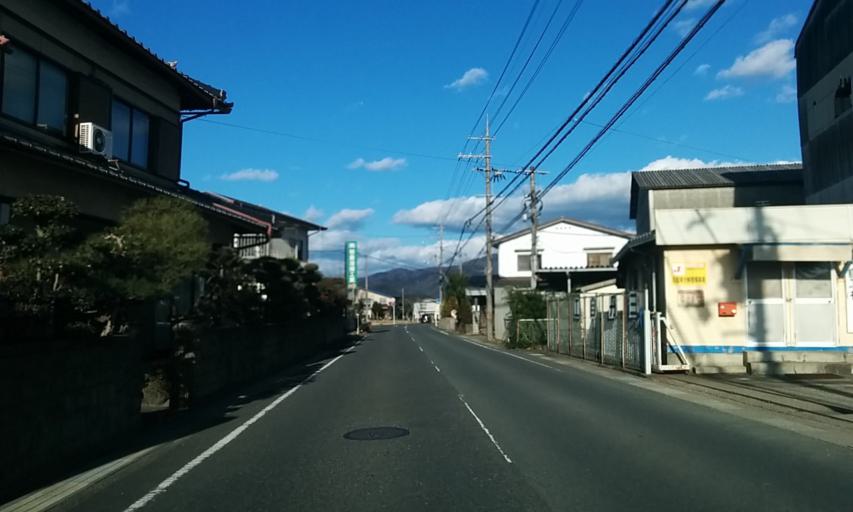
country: JP
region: Kyoto
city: Fukuchiyama
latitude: 35.2982
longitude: 135.0930
